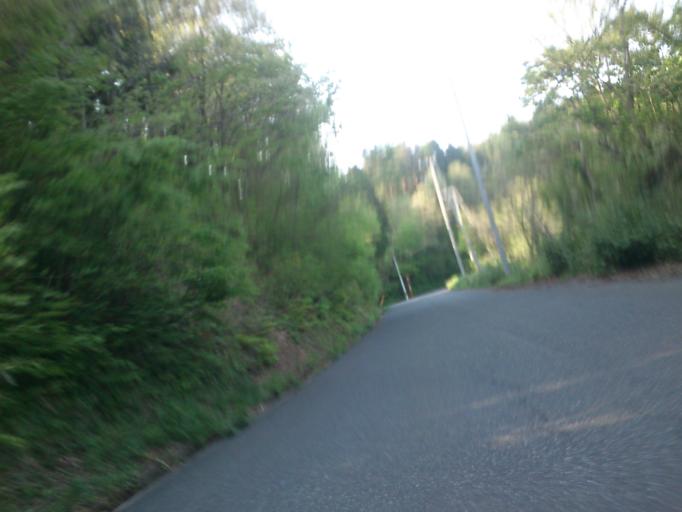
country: JP
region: Kyoto
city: Miyazu
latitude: 35.7079
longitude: 135.1897
